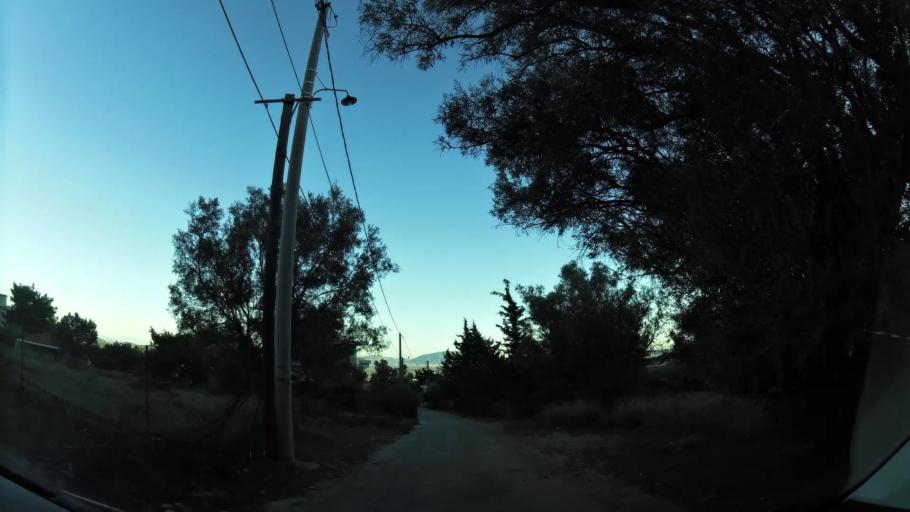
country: GR
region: Attica
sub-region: Nomarchia Anatolikis Attikis
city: Paiania
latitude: 37.9703
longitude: 23.8381
